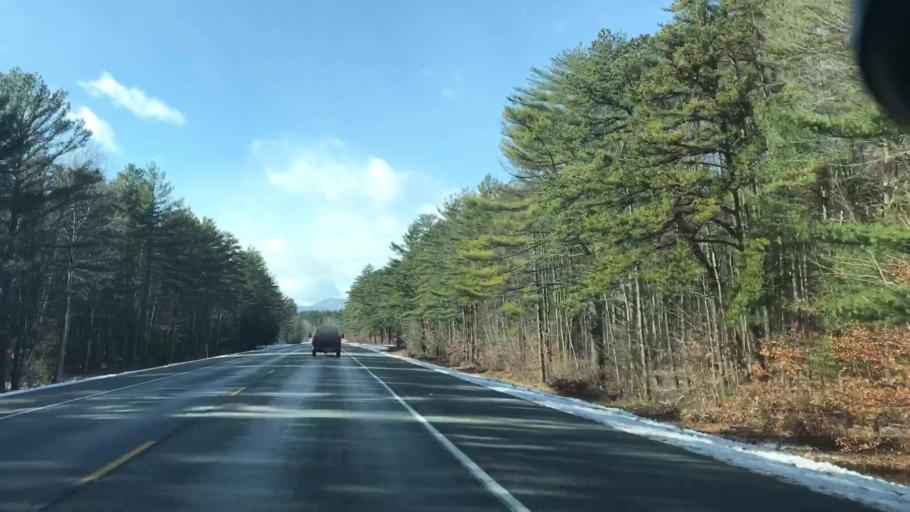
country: US
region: New Hampshire
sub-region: Carroll County
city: Freedom
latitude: 43.7908
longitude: -71.0792
